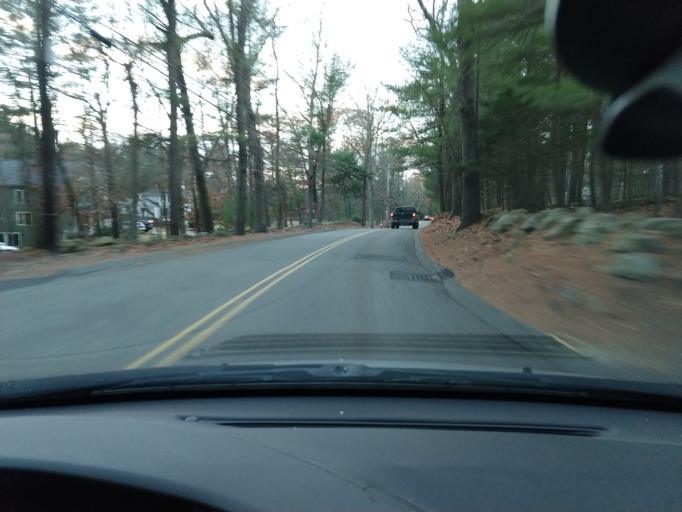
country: US
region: Massachusetts
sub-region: Middlesex County
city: Bedford
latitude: 42.4908
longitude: -71.2496
